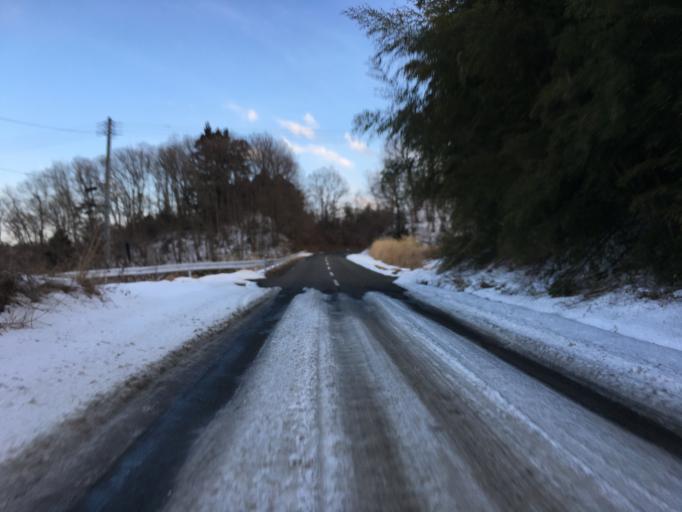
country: JP
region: Fukushima
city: Fukushima-shi
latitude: 37.6508
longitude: 140.5774
